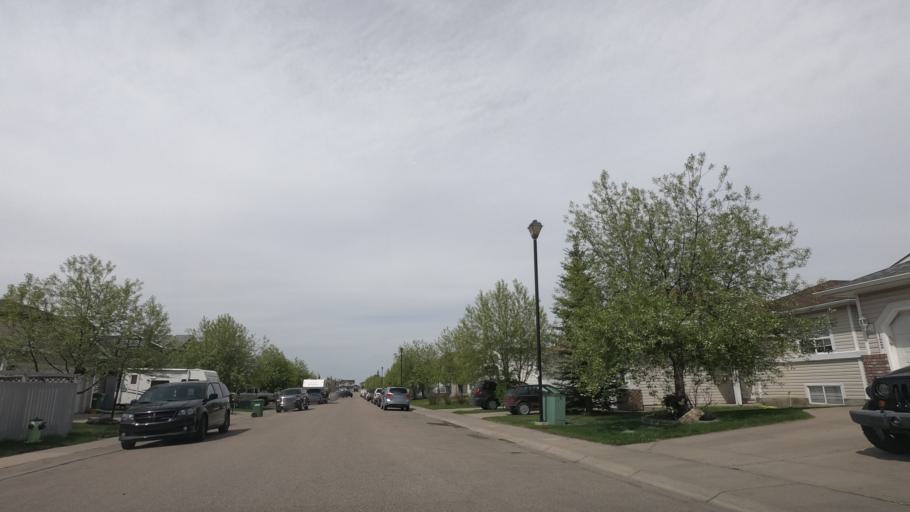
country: CA
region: Alberta
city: Airdrie
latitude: 51.3010
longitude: -114.0207
